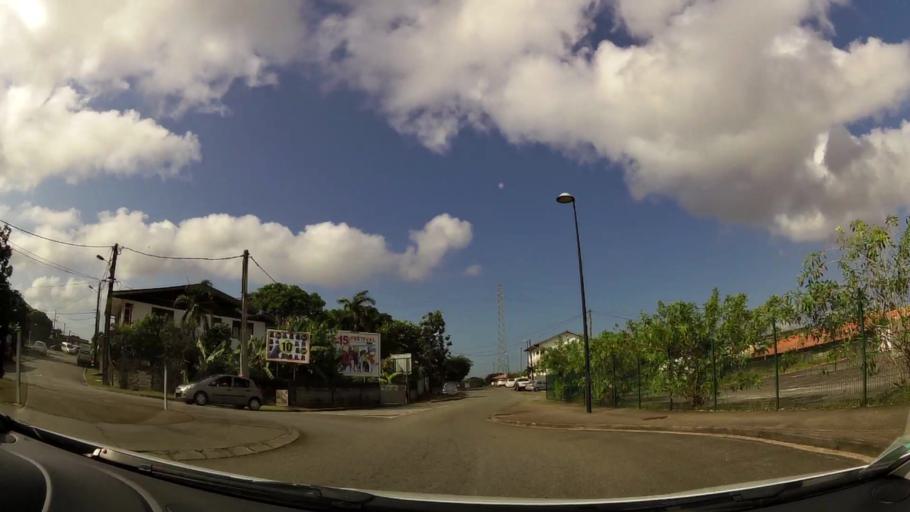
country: GF
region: Guyane
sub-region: Guyane
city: Cayenne
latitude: 4.9285
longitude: -52.3223
